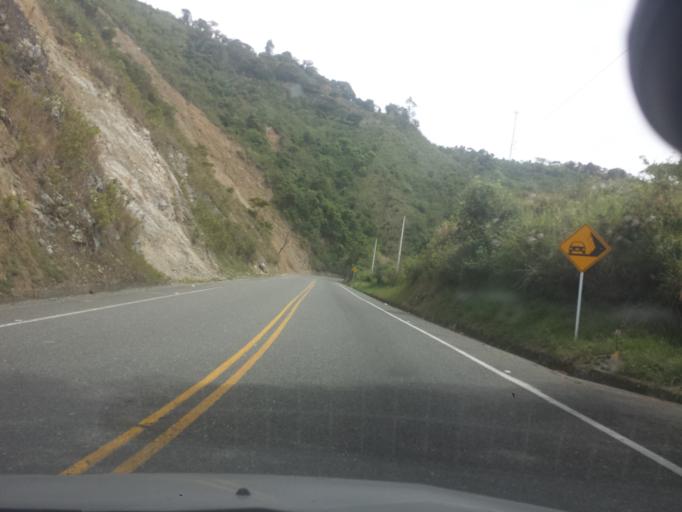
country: CO
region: Antioquia
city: Liborina
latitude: 6.6322
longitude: -75.8718
